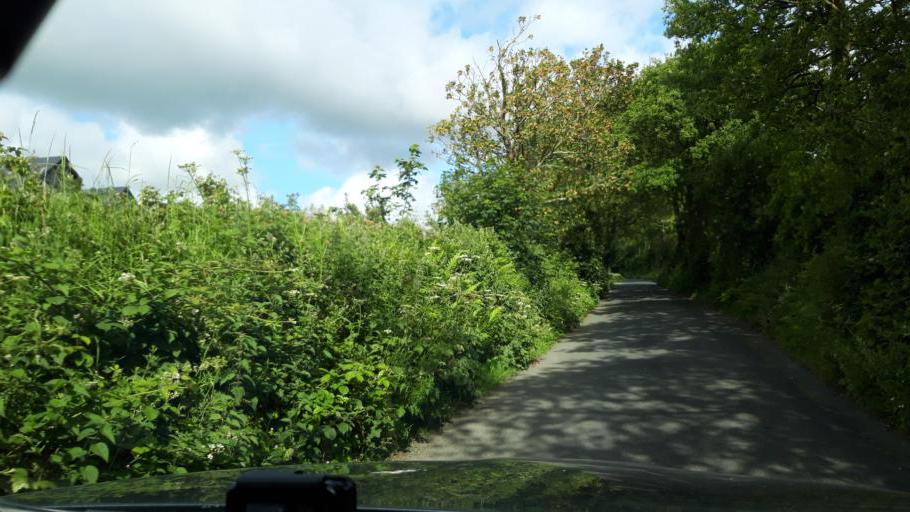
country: IE
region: Leinster
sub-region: Loch Garman
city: Loch Garman
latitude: 52.2852
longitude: -6.5093
